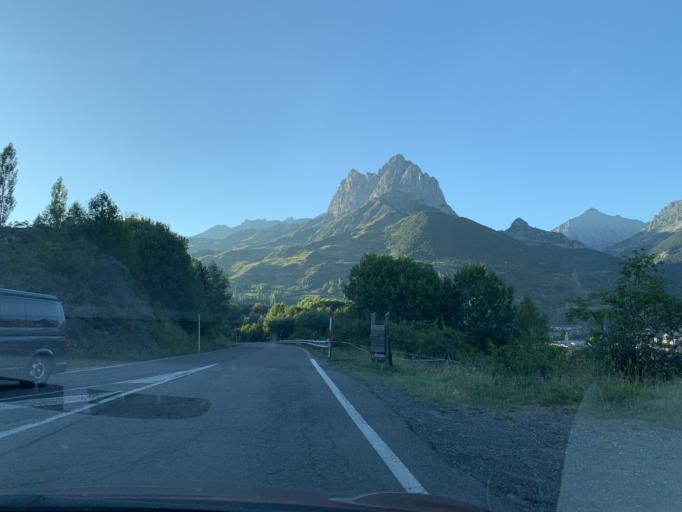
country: ES
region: Aragon
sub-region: Provincia de Huesca
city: Sallent de Gallego
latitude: 42.7610
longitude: -0.3337
